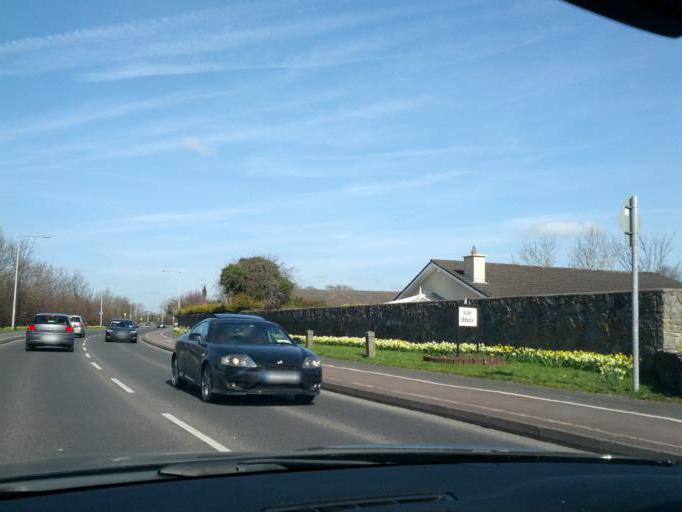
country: IE
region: Leinster
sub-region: Kildare
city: Celbridge
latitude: 53.3529
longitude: -6.5471
